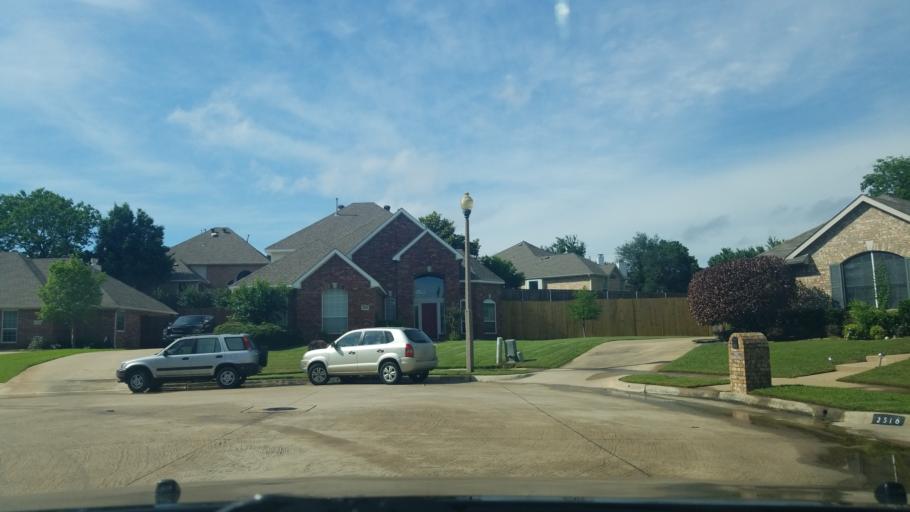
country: US
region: Texas
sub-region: Denton County
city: Denton
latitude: 33.1805
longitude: -97.1050
